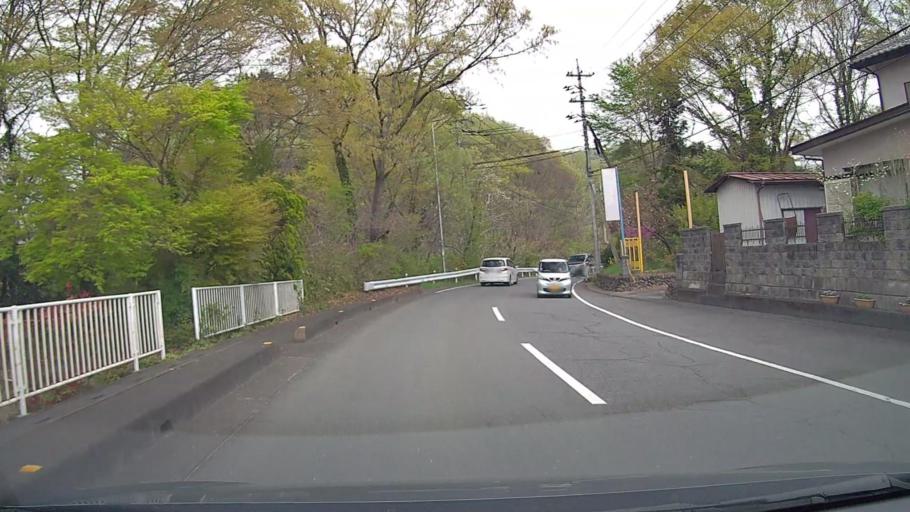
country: JP
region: Saitama
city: Chichibu
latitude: 36.0256
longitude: 139.1191
